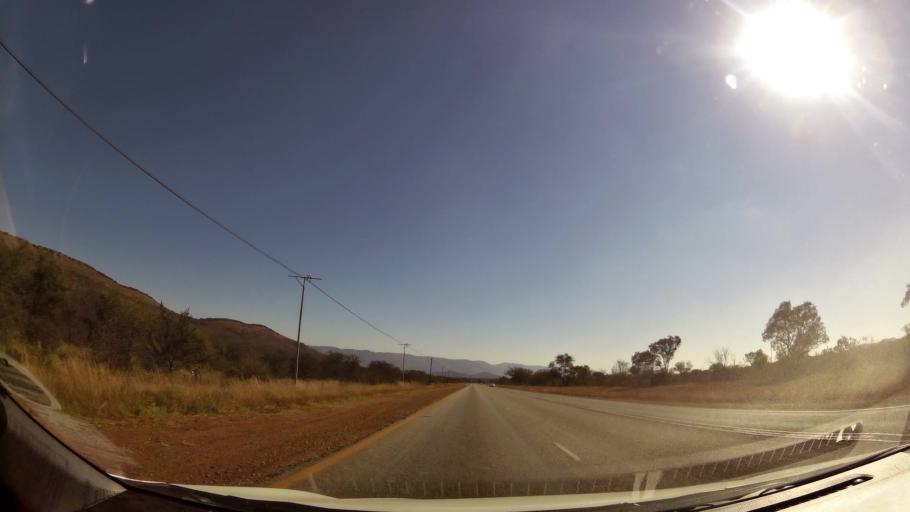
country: ZA
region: Limpopo
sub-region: Waterberg District Municipality
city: Mokopane
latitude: -24.1633
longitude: 29.0613
